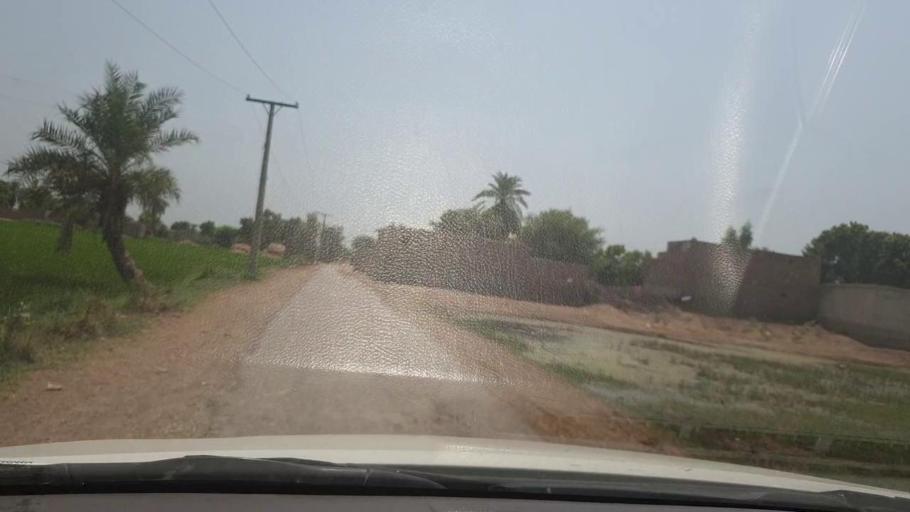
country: PK
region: Sindh
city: Shikarpur
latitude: 28.0693
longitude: 68.5365
